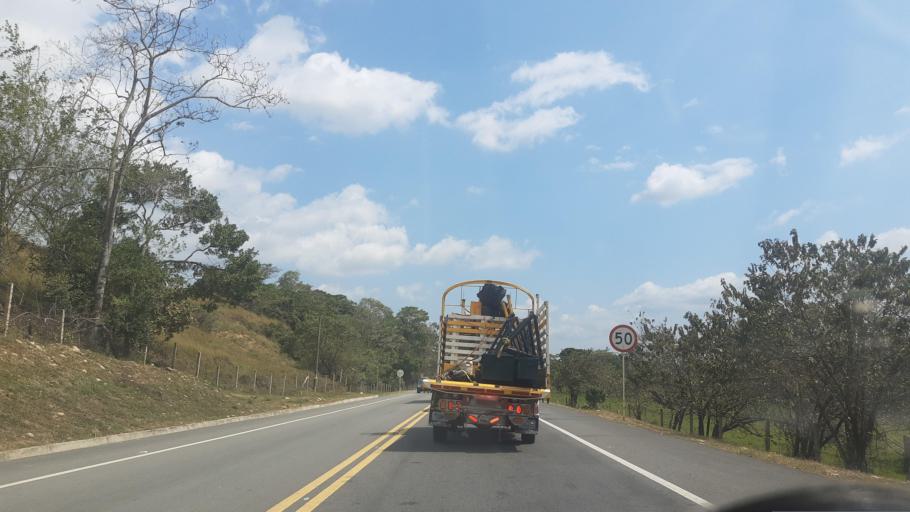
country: CO
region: Casanare
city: Tauramena
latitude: 5.0216
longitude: -72.6600
